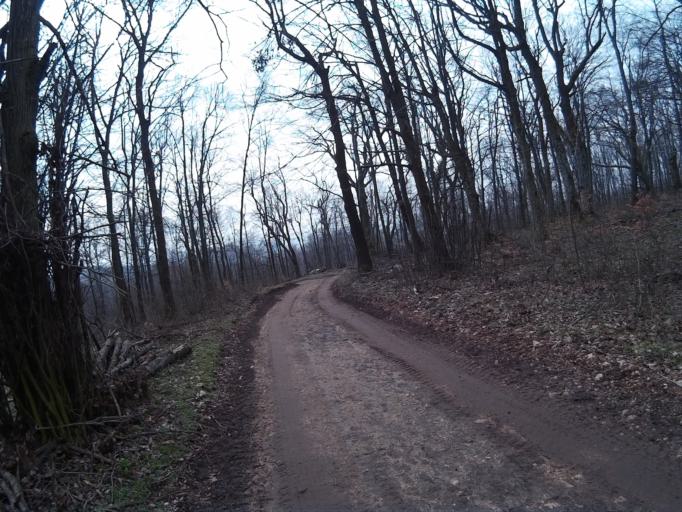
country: HU
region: Veszprem
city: Zirc
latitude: 47.1818
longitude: 17.8449
